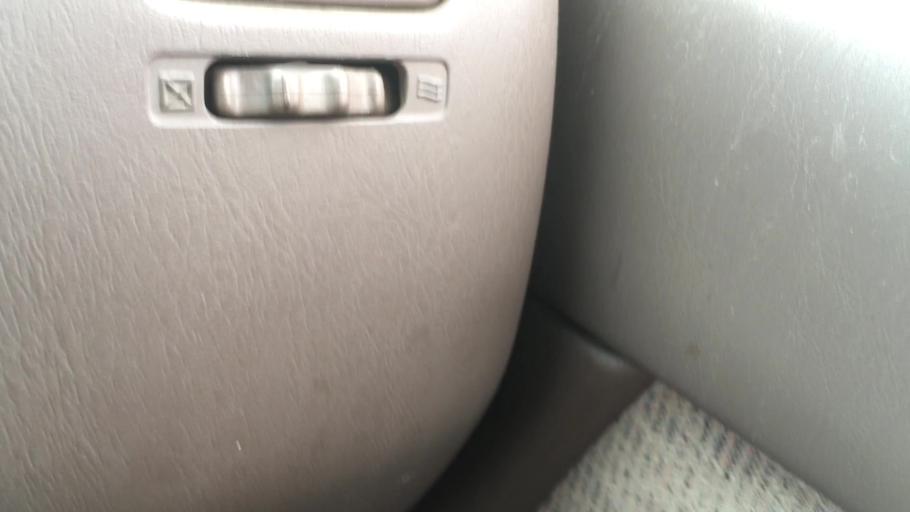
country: US
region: Maryland
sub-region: Worcester County
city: Pocomoke City
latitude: 38.0615
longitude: -75.5478
